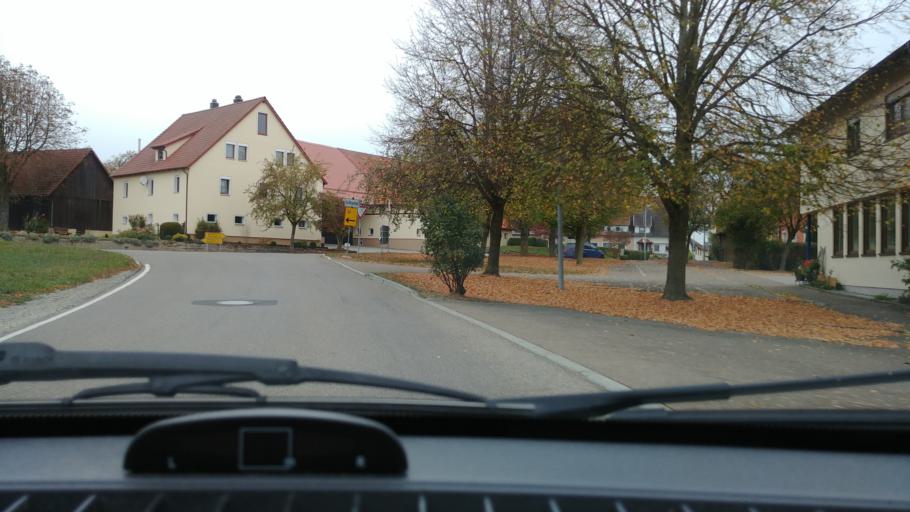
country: DE
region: Bavaria
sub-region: Regierungsbezirk Mittelfranken
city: Insingen
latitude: 49.3462
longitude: 10.0916
